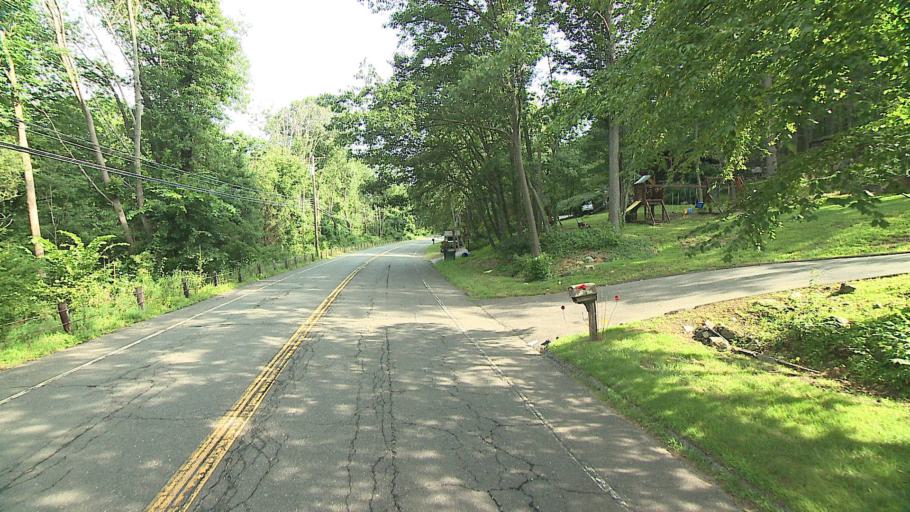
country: US
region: New York
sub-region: Putnam County
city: Putnam Lake
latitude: 41.4767
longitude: -73.4977
